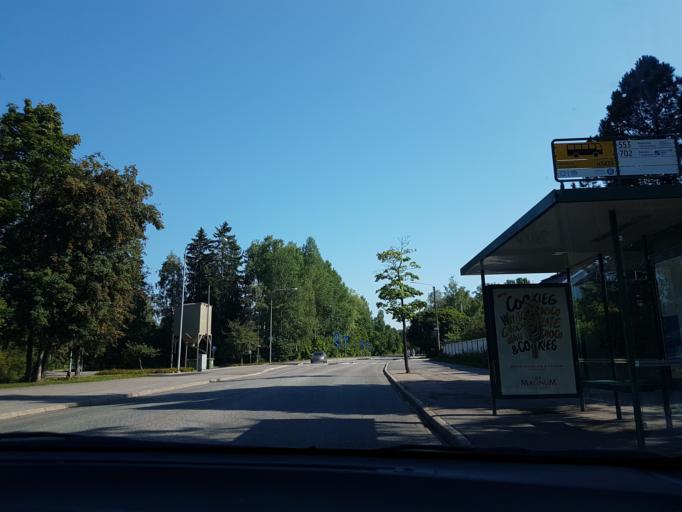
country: FI
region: Uusimaa
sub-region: Helsinki
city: Vantaa
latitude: 60.2676
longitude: 25.0591
